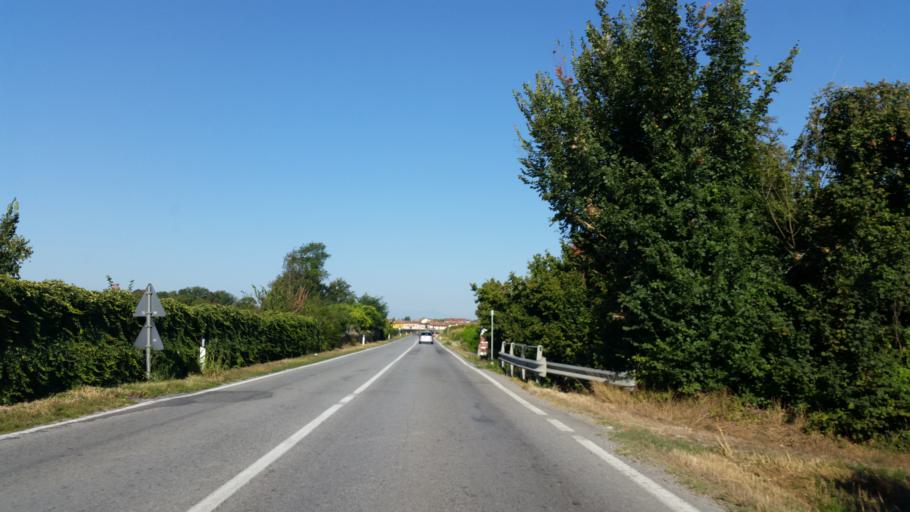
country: IT
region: Piedmont
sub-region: Provincia di Cuneo
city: Cinzano
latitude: 44.6837
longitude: 7.9046
